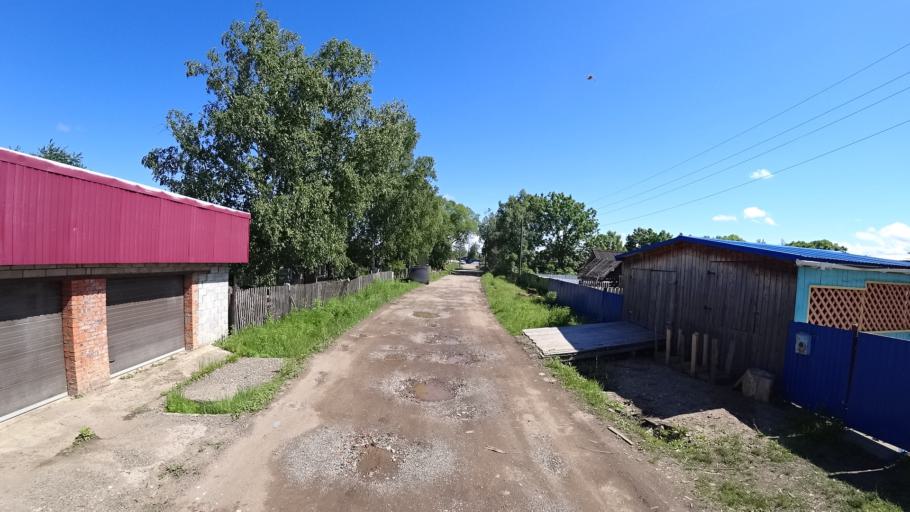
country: RU
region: Khabarovsk Krai
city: Khor
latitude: 47.8872
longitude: 135.0361
